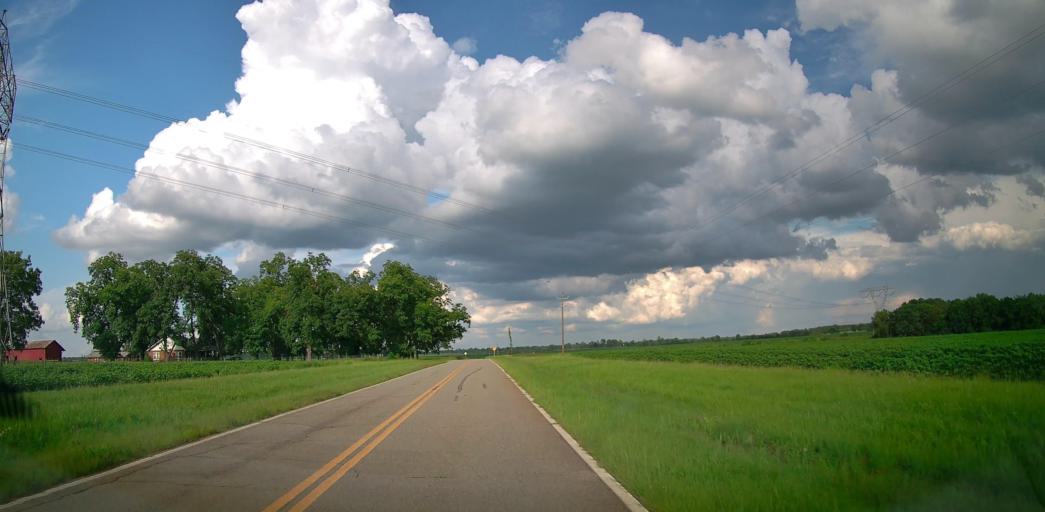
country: US
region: Georgia
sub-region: Bleckley County
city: Cochran
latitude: 32.4067
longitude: -83.4111
